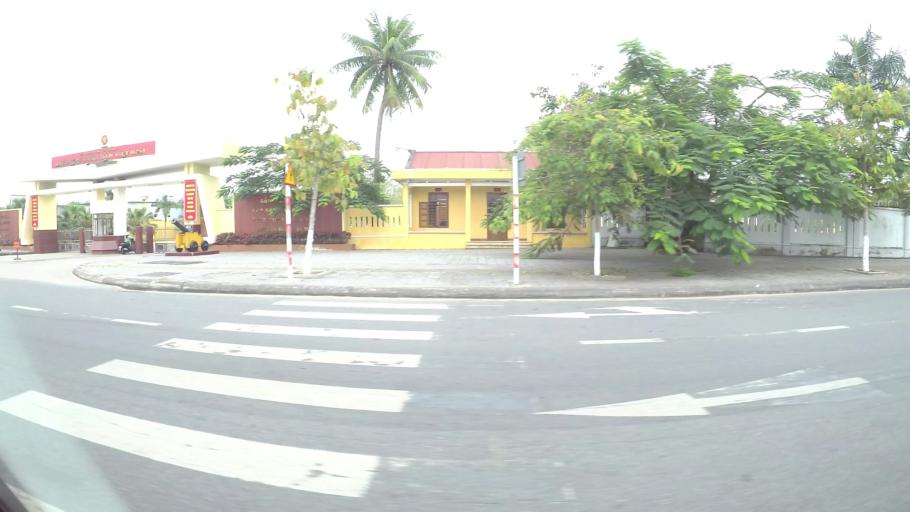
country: VN
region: Da Nang
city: Da Nang
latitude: 16.0508
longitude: 108.2073
